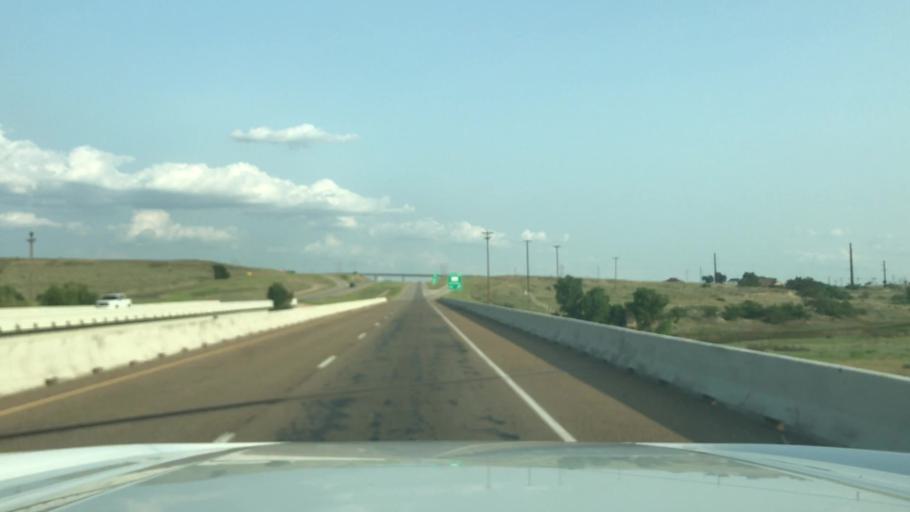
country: US
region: Texas
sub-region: Randall County
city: Canyon
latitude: 35.0055
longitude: -101.9030
